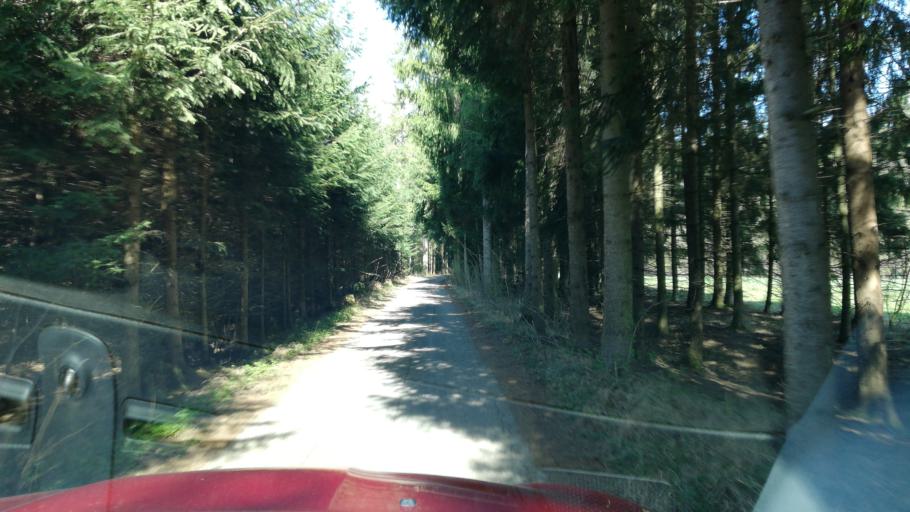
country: AT
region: Upper Austria
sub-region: Wels-Land
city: Sattledt
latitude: 48.0948
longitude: 14.0844
